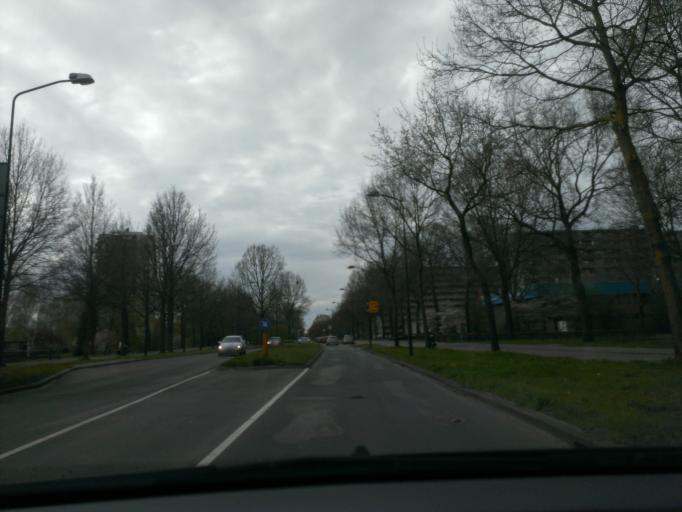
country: NL
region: Gelderland
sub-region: Gemeente Apeldoorn
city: Apeldoorn
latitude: 52.2215
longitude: 5.9978
